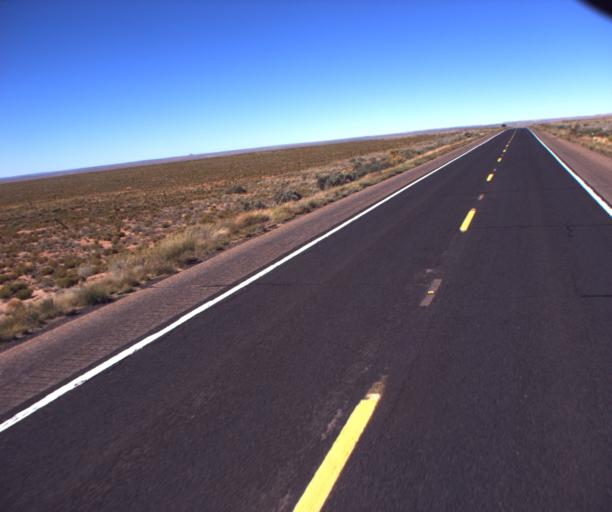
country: US
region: Arizona
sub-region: Navajo County
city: Snowflake
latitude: 34.7058
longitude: -109.7583
